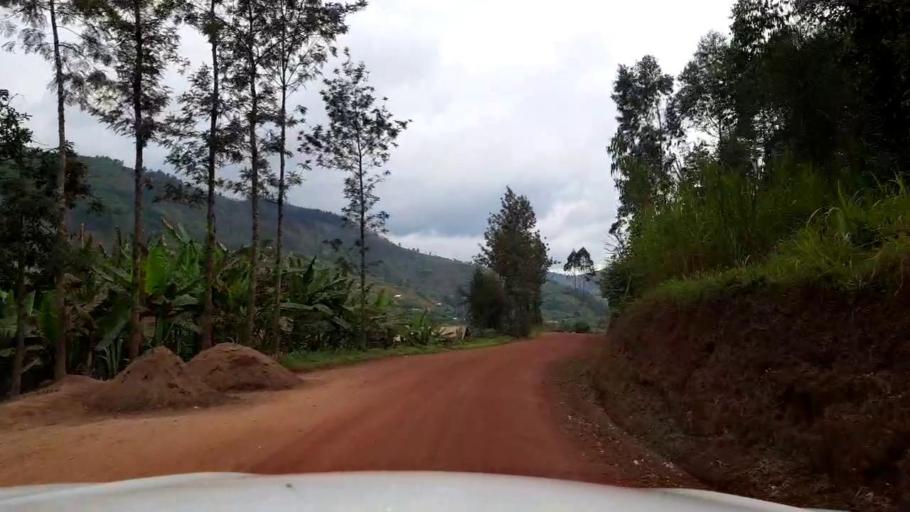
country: RW
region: Northern Province
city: Musanze
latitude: -1.6698
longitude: 29.8008
